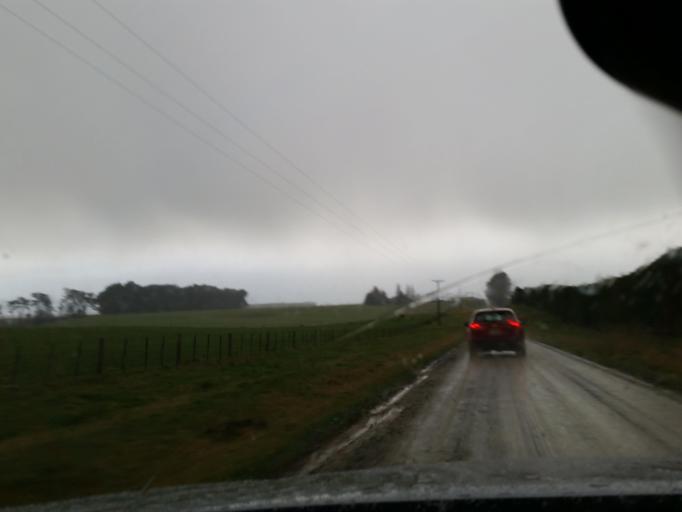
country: NZ
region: Southland
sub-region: Invercargill City
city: Invercargill
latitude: -46.3247
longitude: 168.4534
